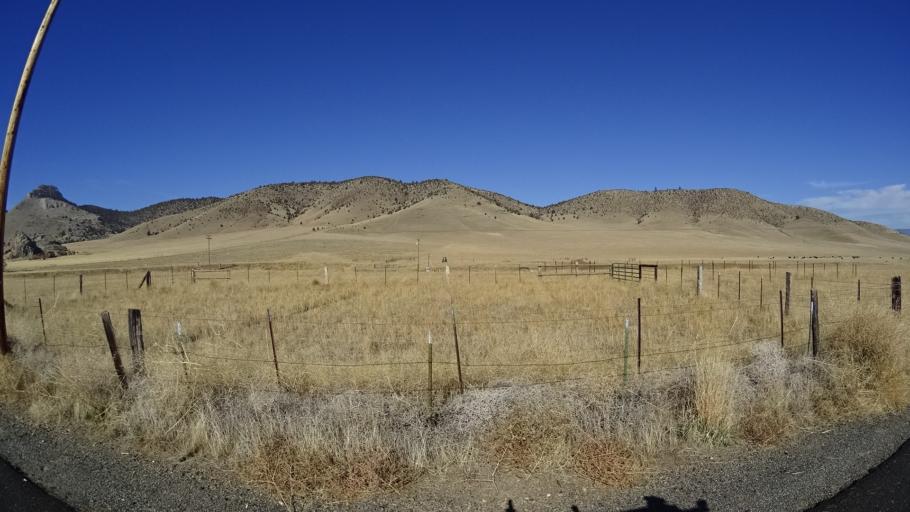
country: US
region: California
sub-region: Siskiyou County
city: Weed
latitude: 41.5035
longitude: -122.5519
